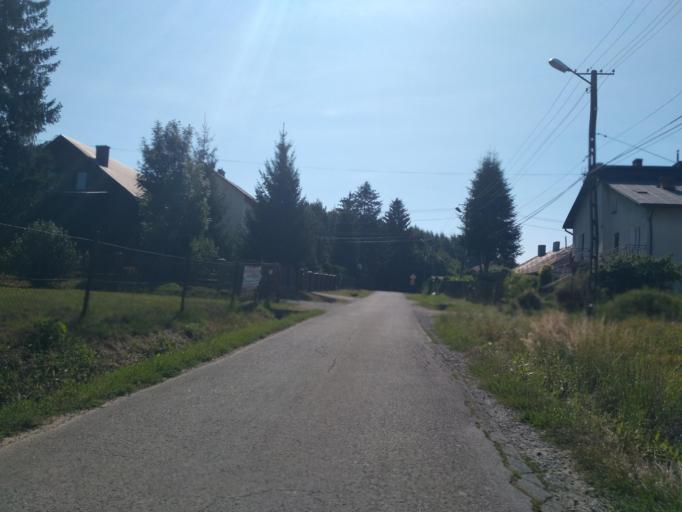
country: PL
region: Subcarpathian Voivodeship
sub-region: Powiat brzozowski
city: Brzozow
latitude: 49.6974
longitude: 22.0326
